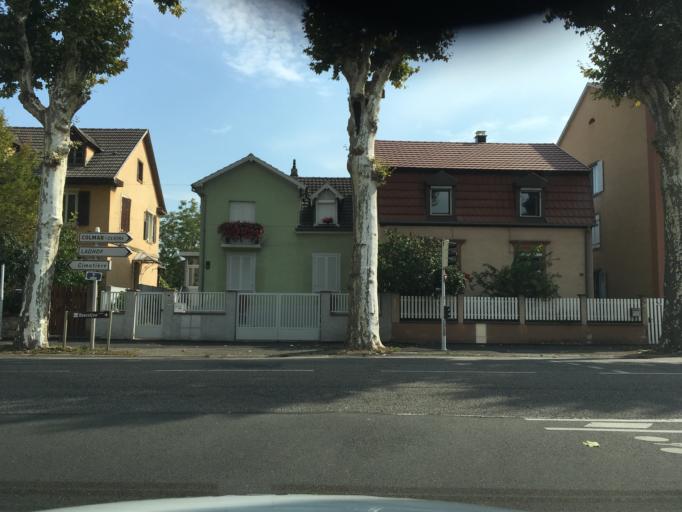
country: FR
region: Alsace
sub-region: Departement du Haut-Rhin
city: Colmar
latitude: 48.0875
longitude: 7.3681
